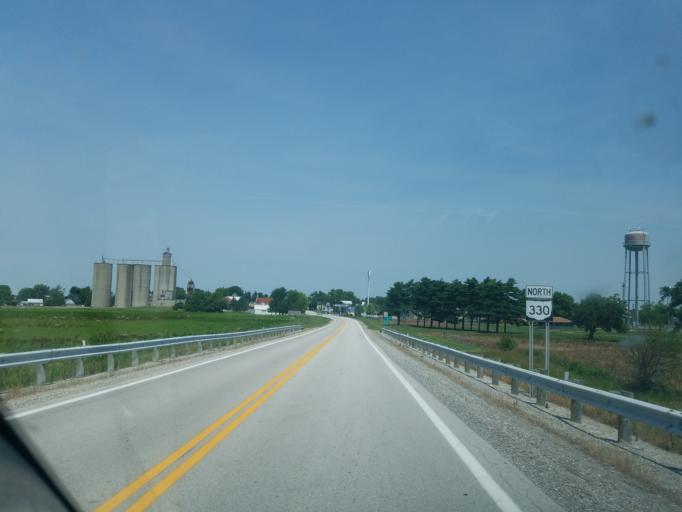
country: US
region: Ohio
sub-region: Wyandot County
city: Carey
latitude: 40.9712
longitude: -83.4828
